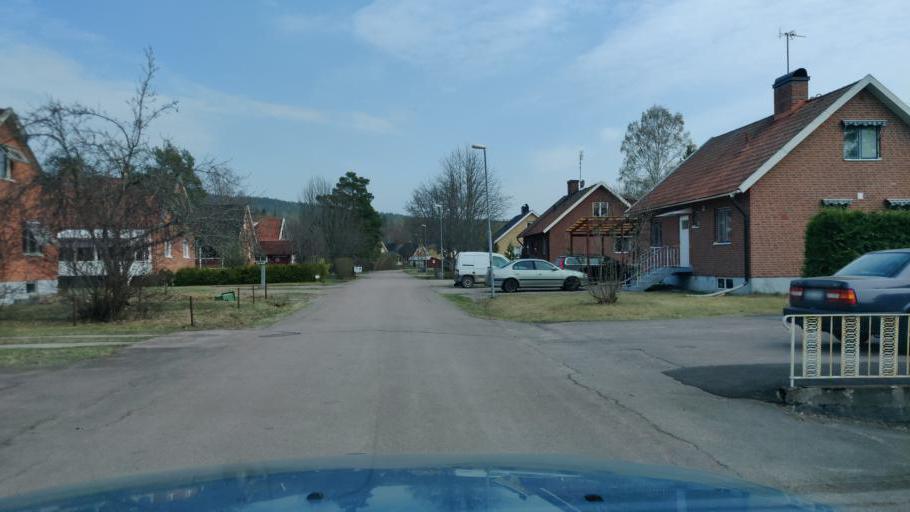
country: SE
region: Vaermland
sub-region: Munkfors Kommun
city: Munkfors
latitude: 59.8741
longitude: 13.5558
